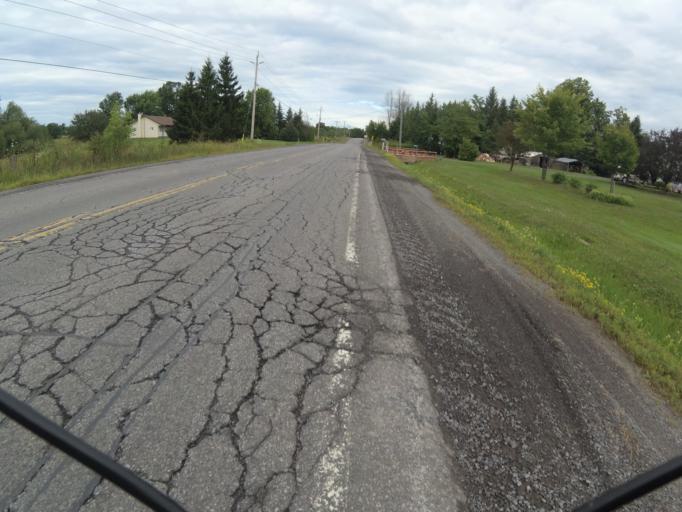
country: CA
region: Ontario
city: Bourget
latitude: 45.3879
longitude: -75.2772
